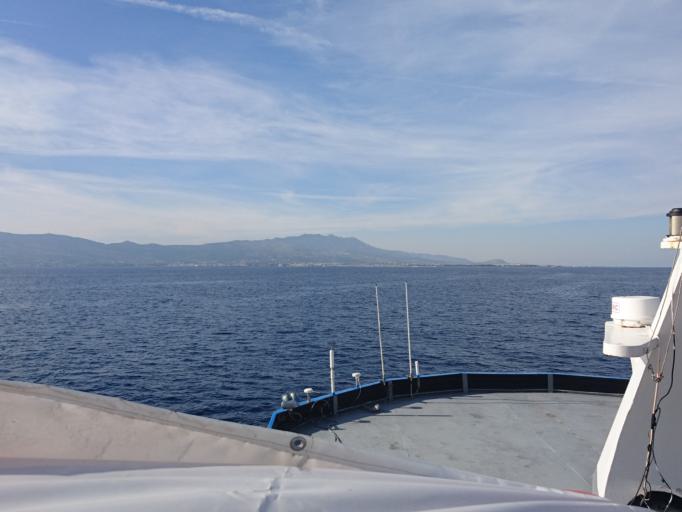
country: GR
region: South Aegean
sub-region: Nomos Dodekanisou
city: Kos
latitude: 36.9353
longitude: 27.3300
